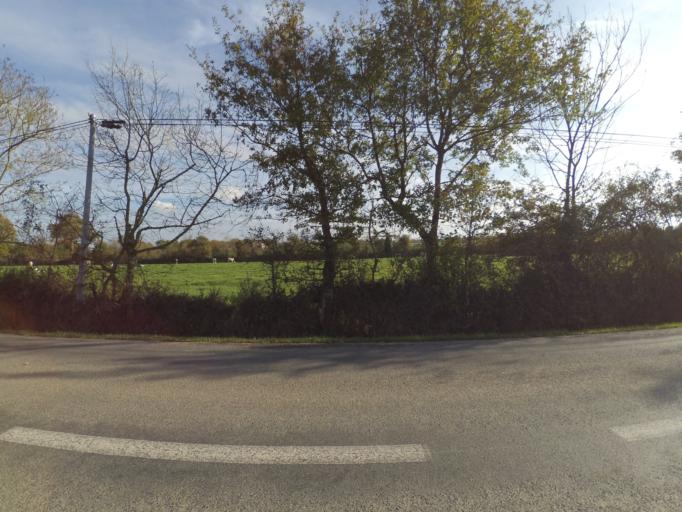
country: FR
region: Pays de la Loire
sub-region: Departement de la Vendee
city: Saint-Hilaire-de-Loulay
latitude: 47.0166
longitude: -1.3447
